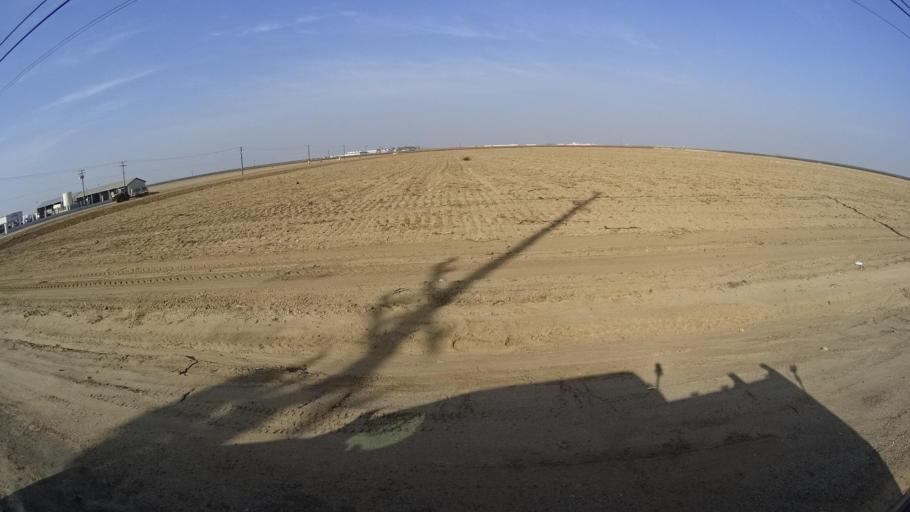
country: US
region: California
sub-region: Tulare County
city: Richgrove
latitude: 35.7760
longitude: -119.1595
